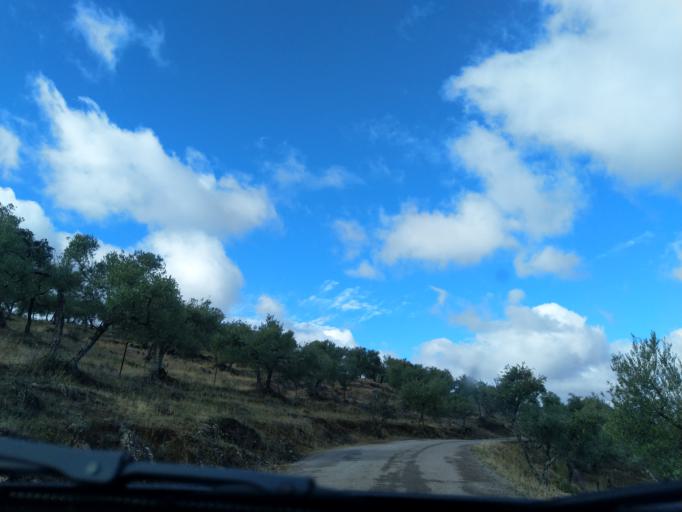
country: ES
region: Extremadura
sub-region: Provincia de Badajoz
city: Reina
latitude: 38.1290
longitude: -5.9303
